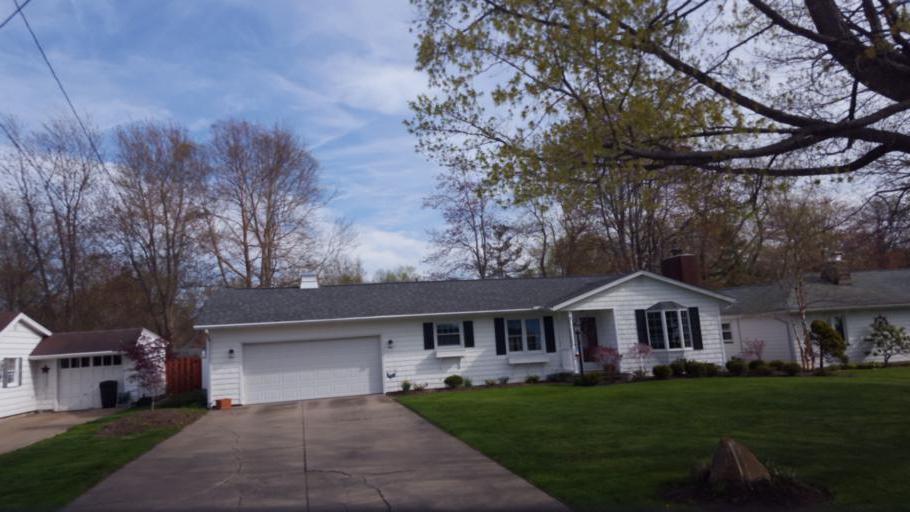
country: US
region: Ohio
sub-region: Ashtabula County
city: Geneva-on-the-Lake
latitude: 41.8482
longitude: -81.0108
